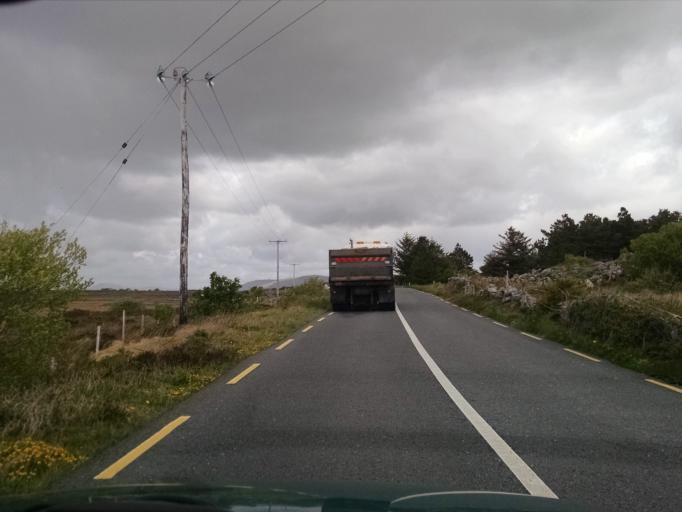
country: IE
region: Connaught
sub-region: County Galway
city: Oughterard
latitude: 53.3095
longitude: -9.5551
